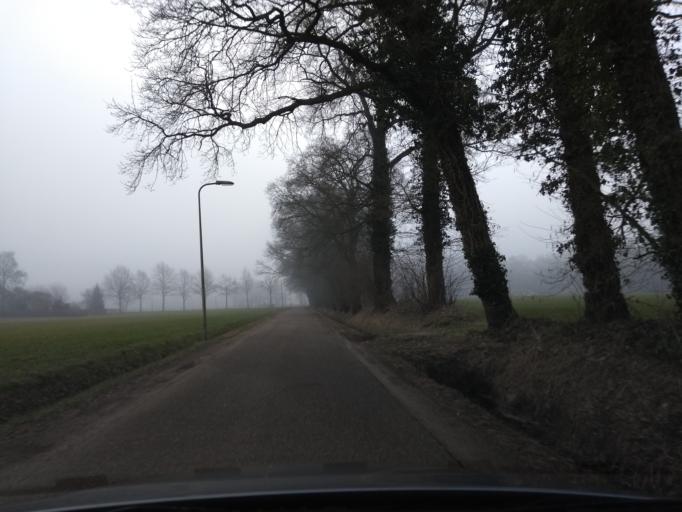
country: NL
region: Overijssel
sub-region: Gemeente Hof van Twente
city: Delden
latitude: 52.2485
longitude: 6.7314
